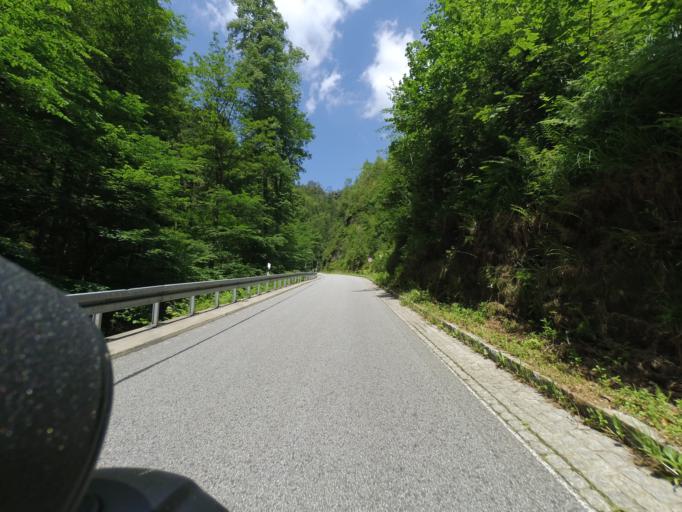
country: DE
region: Saxony
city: Porschdorf
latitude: 50.9562
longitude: 14.1317
